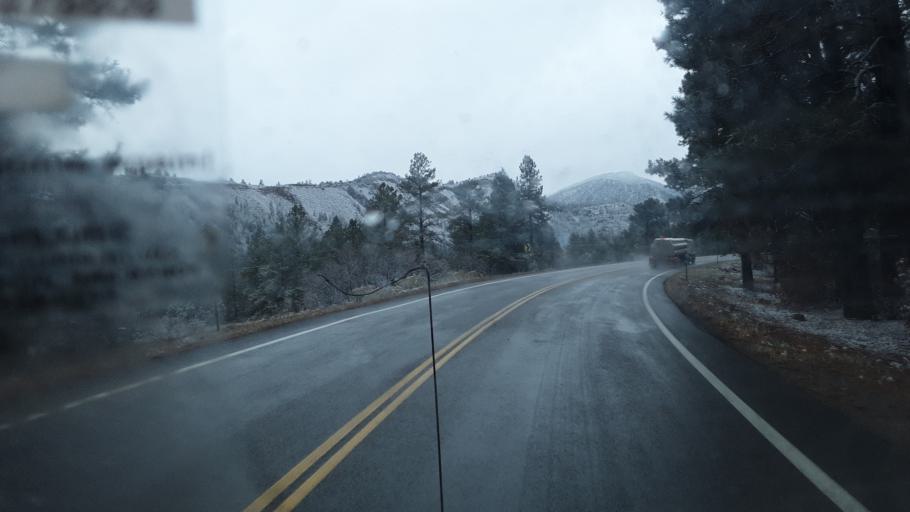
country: US
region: Colorado
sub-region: La Plata County
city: Bayfield
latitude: 37.2046
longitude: -107.3338
